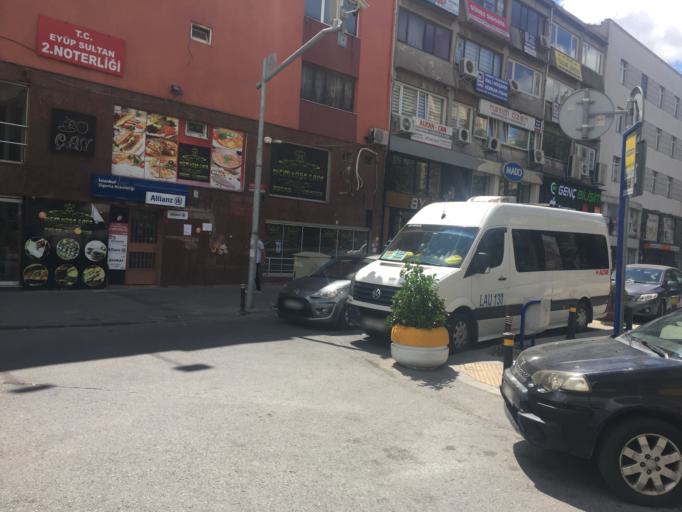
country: TR
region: Istanbul
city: merter keresteciler
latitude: 41.0345
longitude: 28.9119
